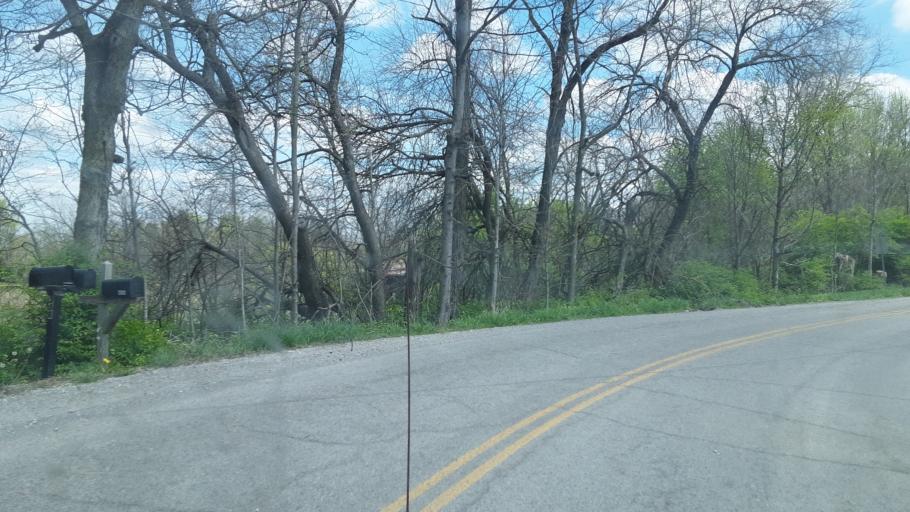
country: US
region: Kentucky
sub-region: Owen County
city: Owenton
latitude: 38.6399
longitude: -84.7754
